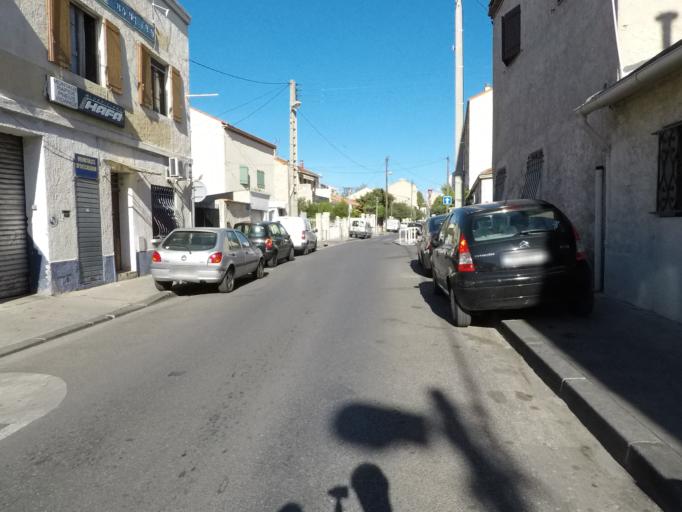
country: FR
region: Provence-Alpes-Cote d'Azur
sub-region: Departement des Bouches-du-Rhone
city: Marseille 10
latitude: 43.2779
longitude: 5.4141
